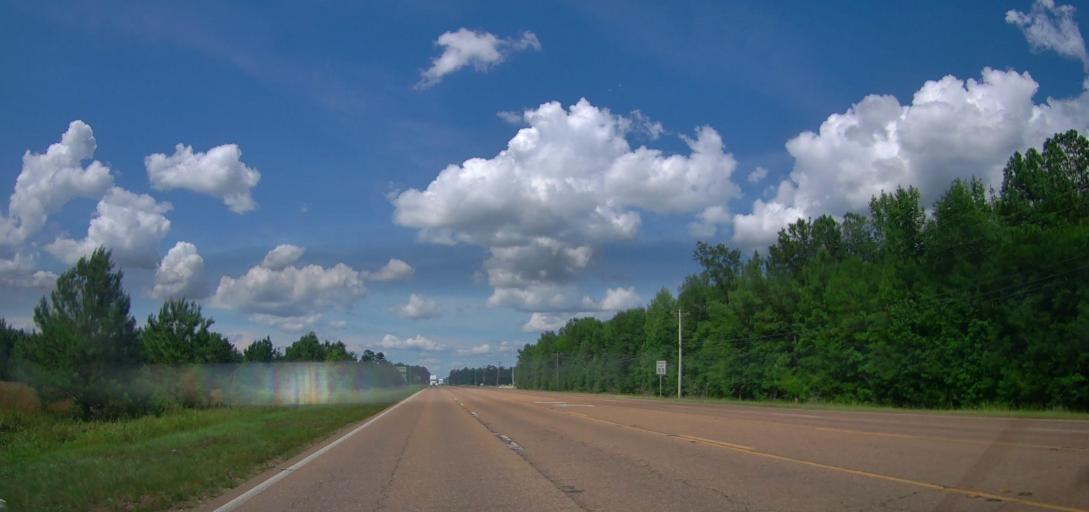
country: US
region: Mississippi
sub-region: Lowndes County
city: Columbus Air Force Base
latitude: 33.5731
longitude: -88.4308
